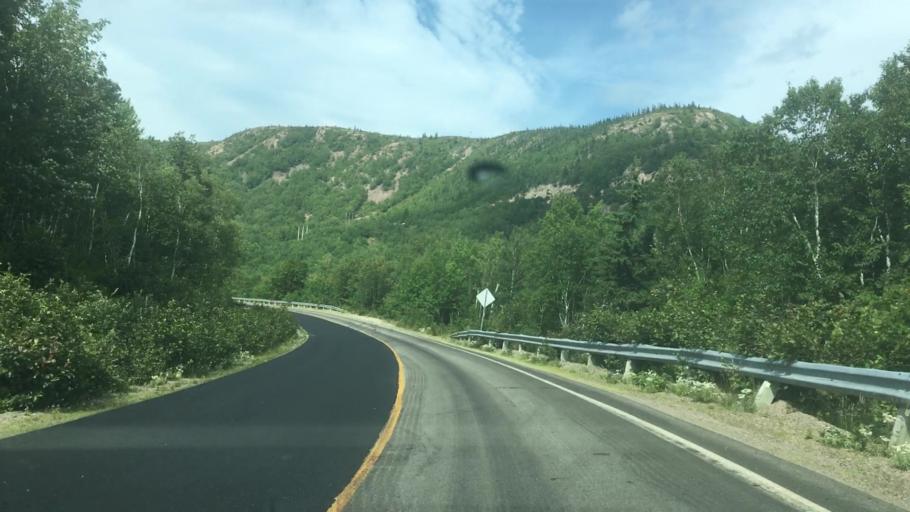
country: CA
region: Nova Scotia
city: Sydney Mines
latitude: 46.5777
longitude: -60.3891
